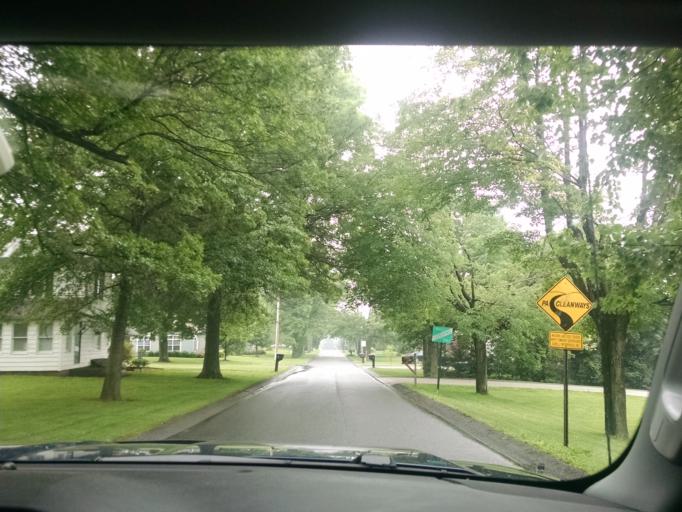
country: US
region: Pennsylvania
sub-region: Indiana County
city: Chevy Chase Heights
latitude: 40.6419
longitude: -79.1354
